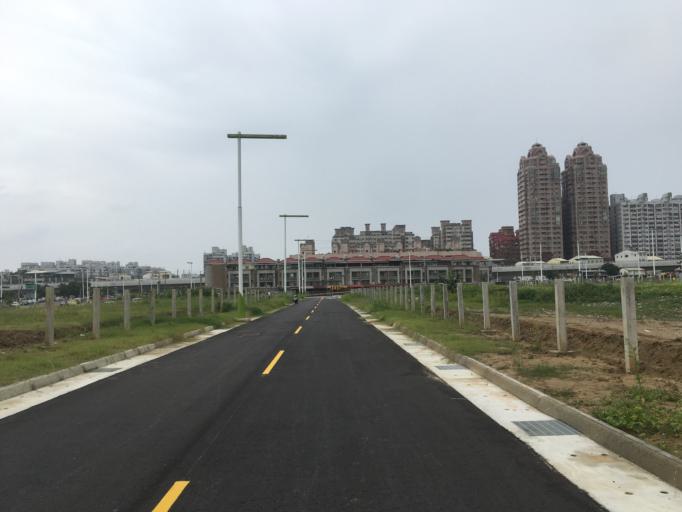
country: TW
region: Taiwan
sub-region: Taichung City
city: Taichung
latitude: 24.1872
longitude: 120.7060
